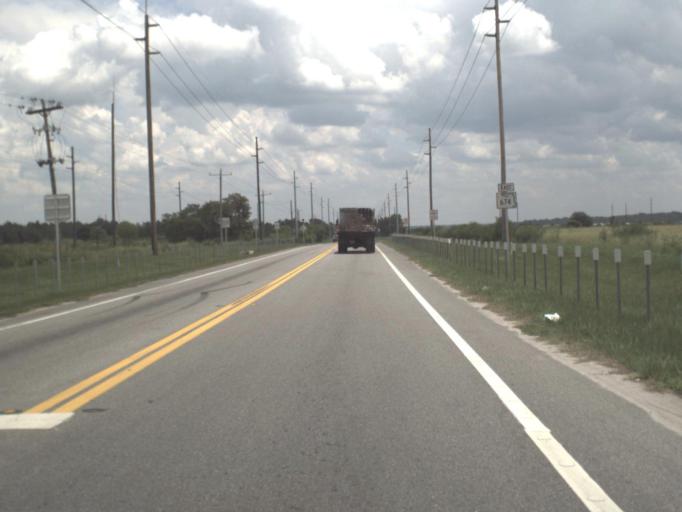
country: US
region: Florida
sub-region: Hillsborough County
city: Balm
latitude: 27.7045
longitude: -82.1460
